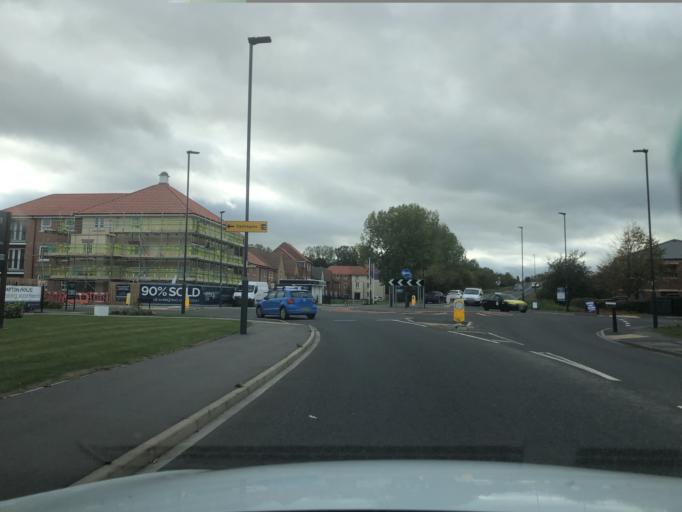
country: GB
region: England
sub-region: North Yorkshire
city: Northallerton
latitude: 54.3457
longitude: -1.4456
